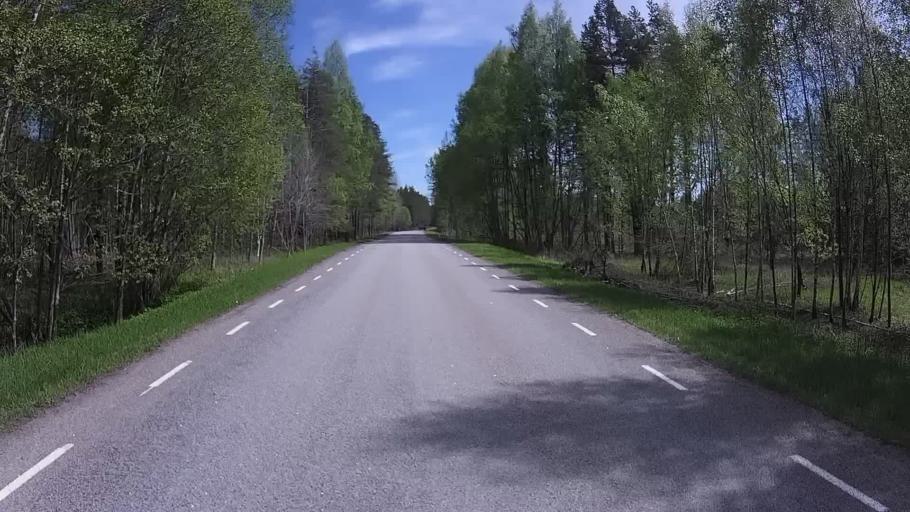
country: LV
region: Apes Novads
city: Ape
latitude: 57.6080
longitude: 26.4552
